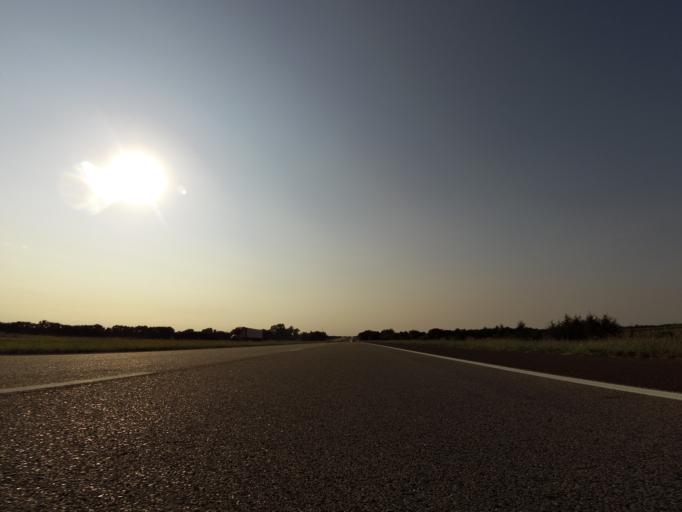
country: US
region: Kansas
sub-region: Reno County
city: Haven
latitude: 37.9254
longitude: -97.8403
